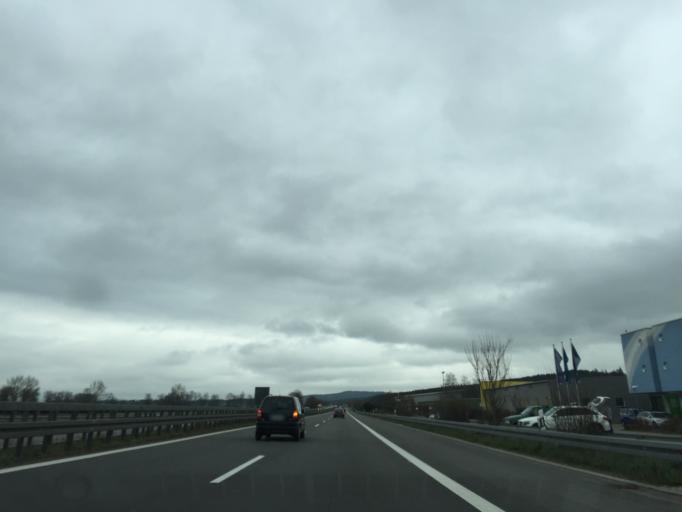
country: DE
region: Baden-Wuerttemberg
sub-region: Freiburg Region
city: Donaueschingen
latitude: 47.9756
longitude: 8.5148
